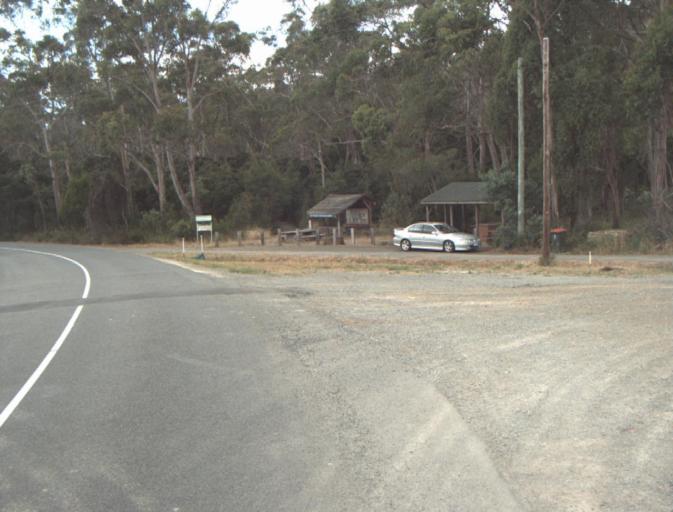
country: AU
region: Tasmania
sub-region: Launceston
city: Mayfield
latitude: -41.2426
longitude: 147.0170
